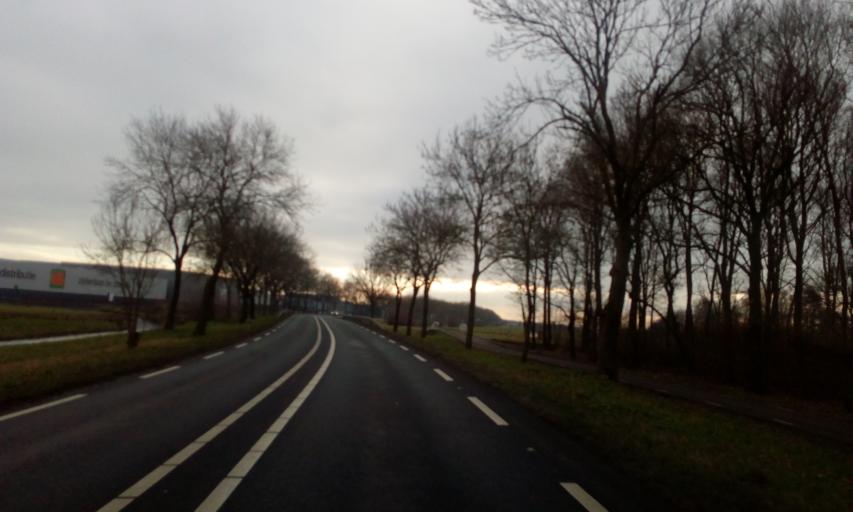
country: NL
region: South Holland
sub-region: Gemeente Vlist
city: Haastrecht
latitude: 51.9683
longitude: 4.7706
